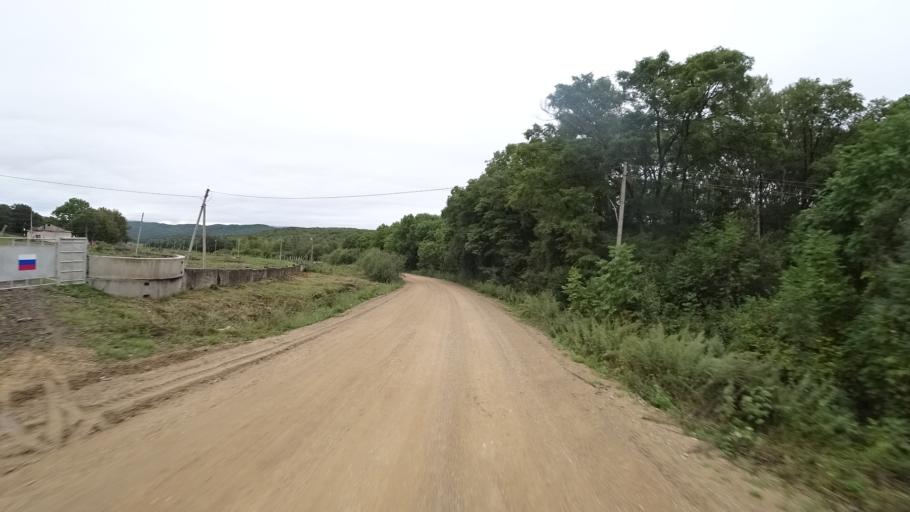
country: RU
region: Primorskiy
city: Rettikhovka
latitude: 44.1778
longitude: 132.8521
